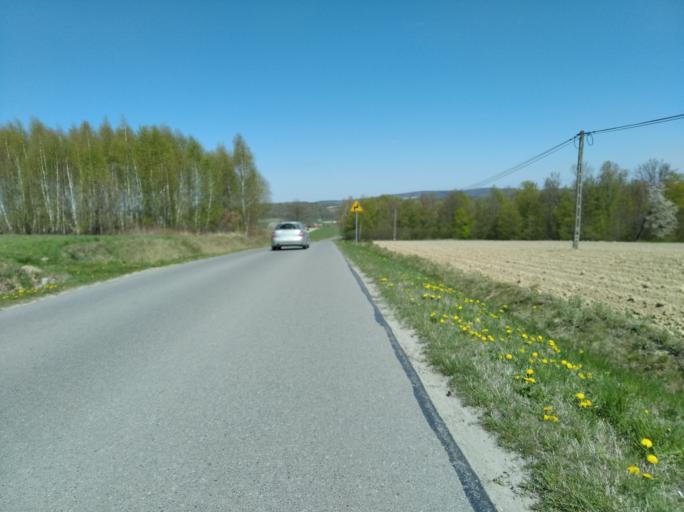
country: PL
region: Subcarpathian Voivodeship
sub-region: Powiat strzyzowski
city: Wisniowa
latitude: 49.9004
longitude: 21.6687
